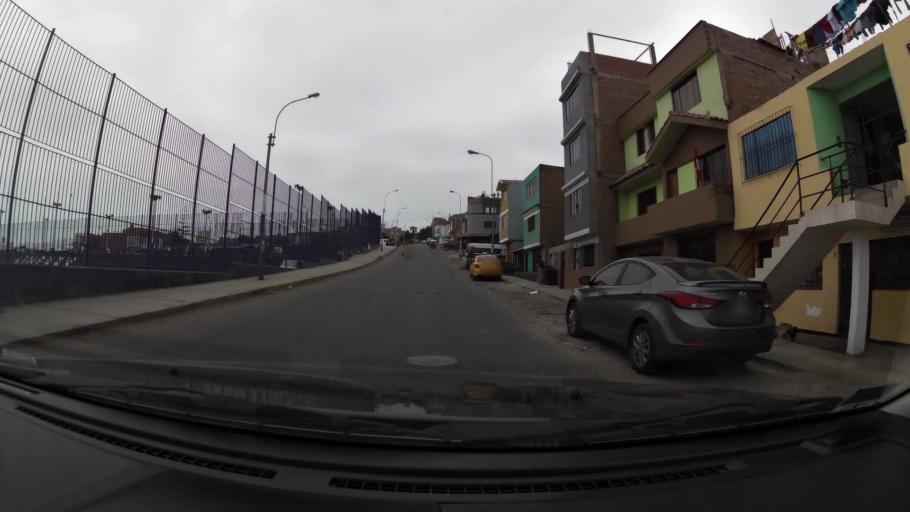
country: PE
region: Lima
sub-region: Lima
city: Surco
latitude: -12.1940
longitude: -76.9874
